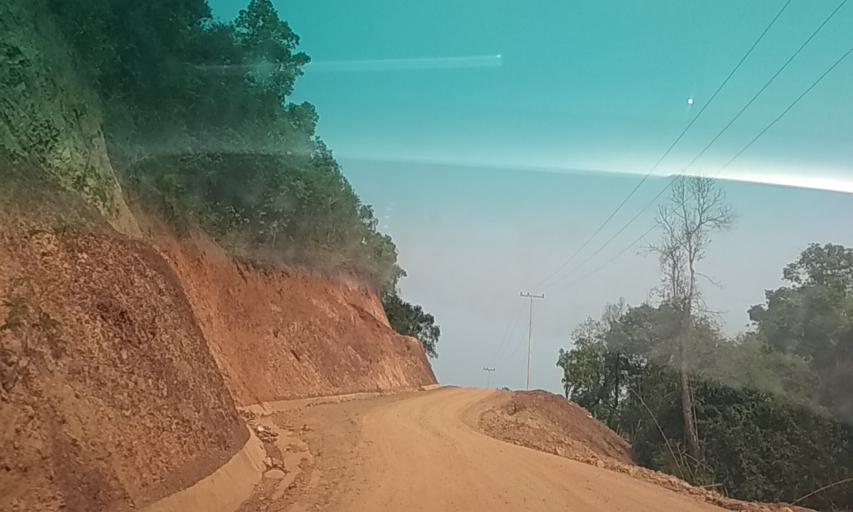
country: VN
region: Huyen Dien Bien
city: Dien Bien Phu
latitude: 21.4594
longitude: 102.7728
